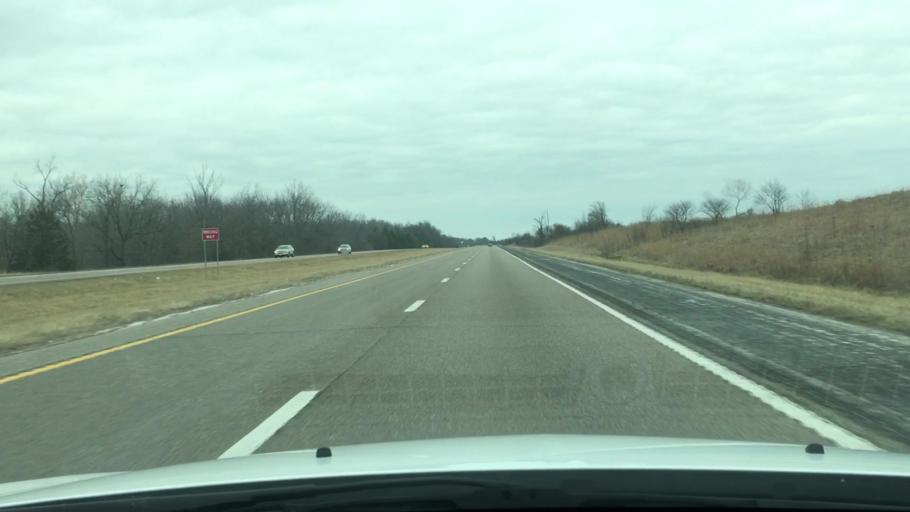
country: US
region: Missouri
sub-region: Callaway County
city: Fulton
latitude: 38.9894
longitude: -91.8937
